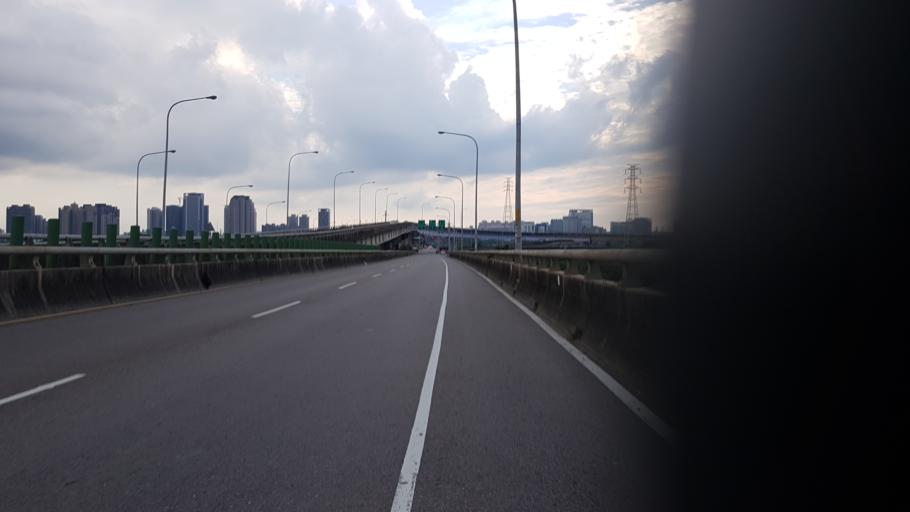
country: TW
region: Taiwan
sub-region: Hsinchu
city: Zhubei
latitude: 24.8084
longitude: 121.0195
